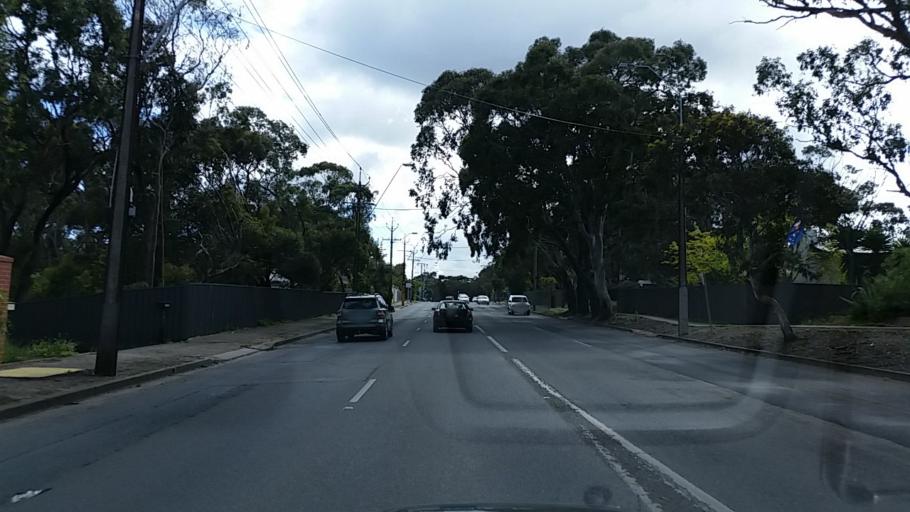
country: AU
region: South Australia
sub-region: Mitcham
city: Blackwood
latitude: -35.0249
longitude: 138.6053
